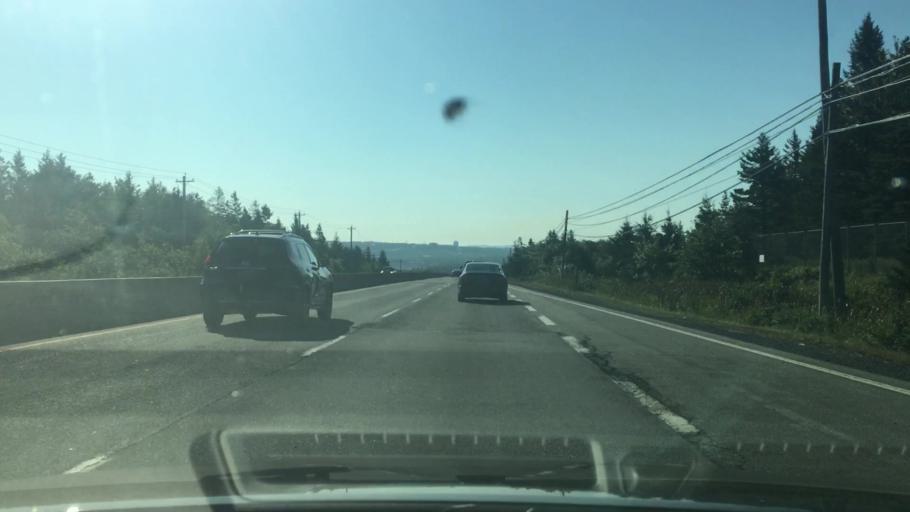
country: CA
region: Nova Scotia
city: Dartmouth
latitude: 44.7175
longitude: -63.6345
